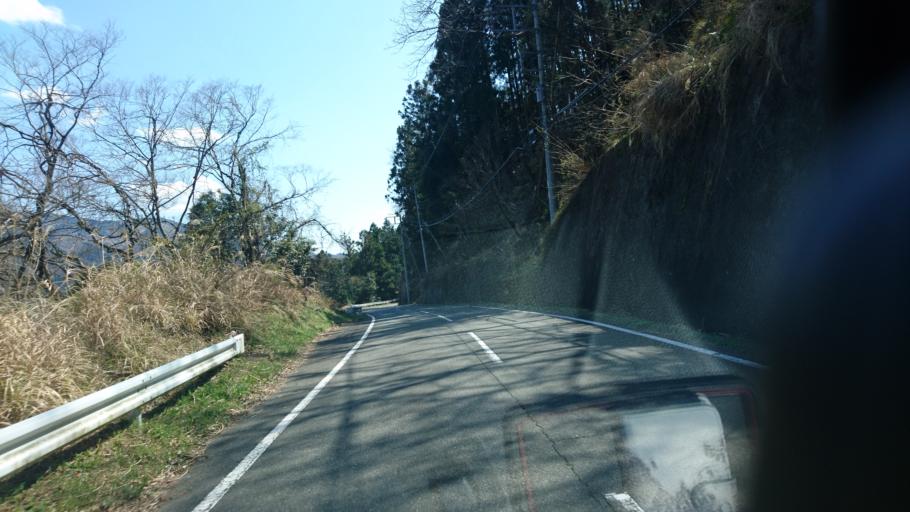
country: JP
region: Shizuoka
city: Fujinomiya
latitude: 35.3500
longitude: 138.4375
